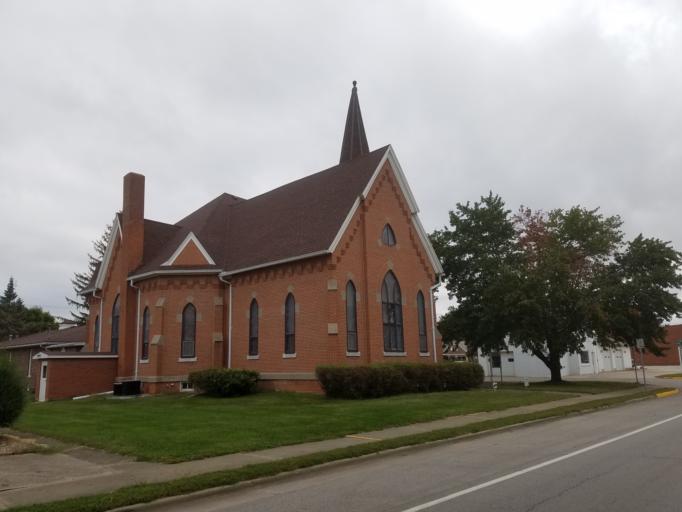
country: US
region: Illinois
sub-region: Fulton County
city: Astoria
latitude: 40.3513
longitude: -90.3246
